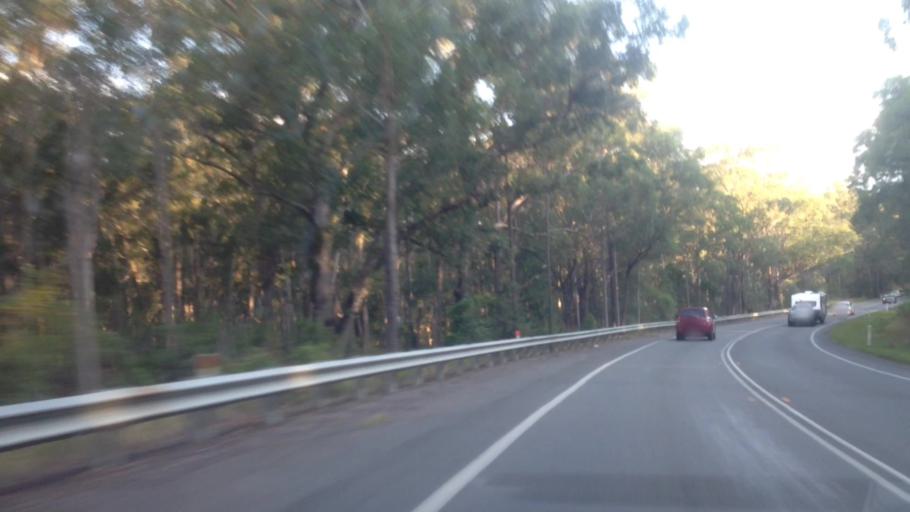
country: AU
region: New South Wales
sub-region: Lake Macquarie Shire
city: Dora Creek
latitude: -32.9973
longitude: 151.4928
